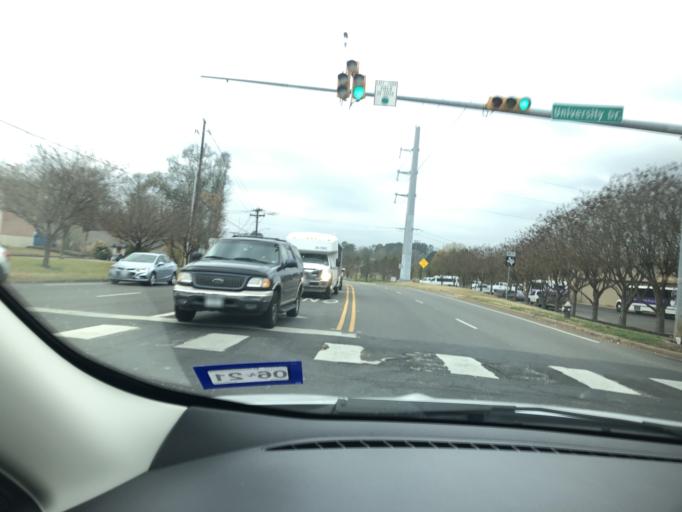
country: US
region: Texas
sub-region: Nacogdoches County
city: Nacogdoches
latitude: 31.6182
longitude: -94.6396
